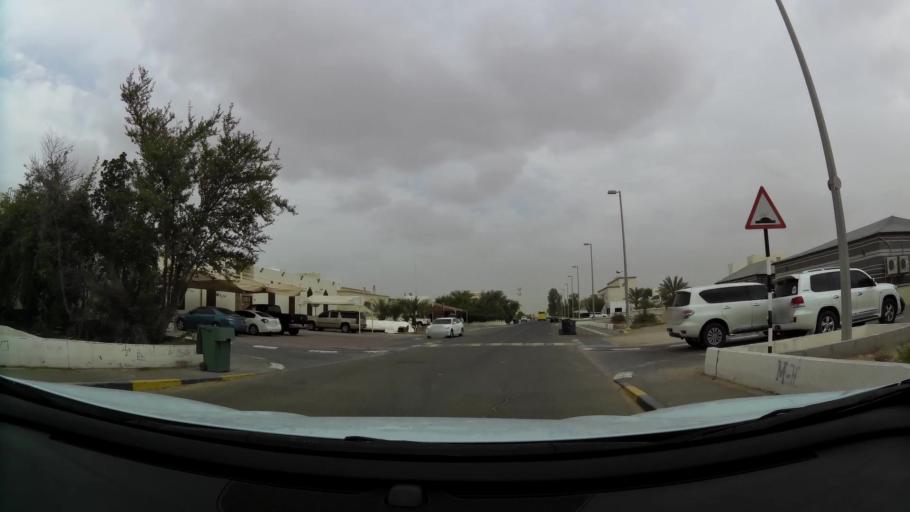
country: AE
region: Abu Dhabi
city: Abu Dhabi
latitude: 24.3452
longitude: 54.6462
